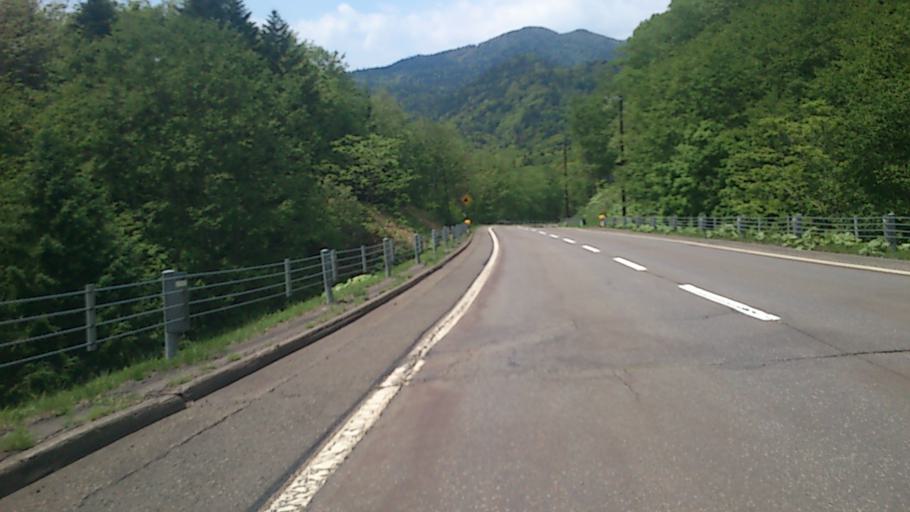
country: JP
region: Hokkaido
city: Otofuke
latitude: 43.3697
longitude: 143.1956
